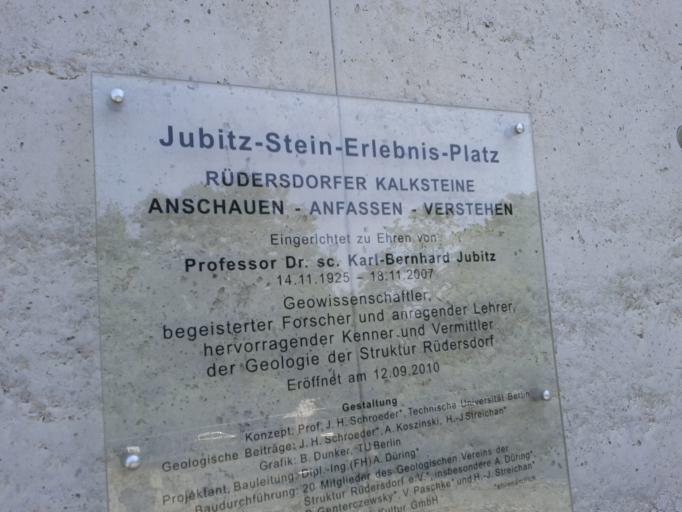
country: DE
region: Brandenburg
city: Woltersdorf
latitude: 52.4768
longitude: 13.7798
